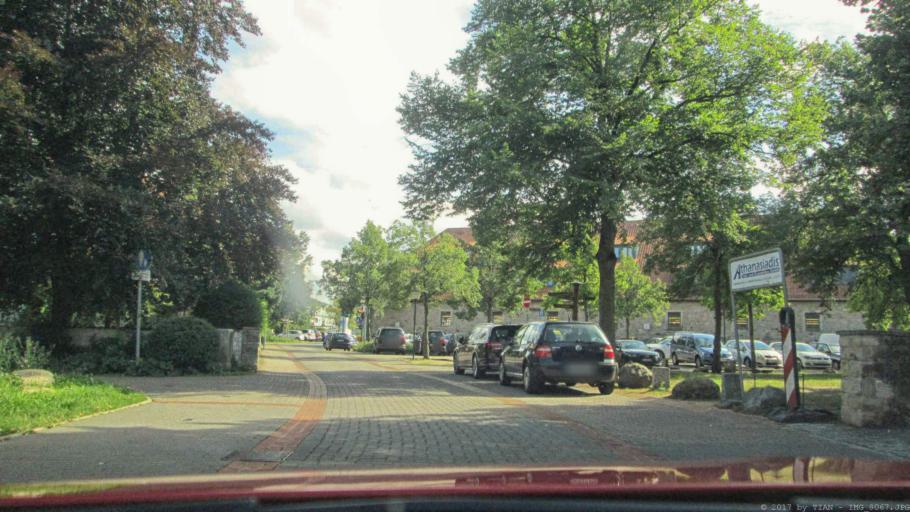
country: DE
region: Lower Saxony
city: Weyhausen
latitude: 52.4178
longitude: 10.7151
